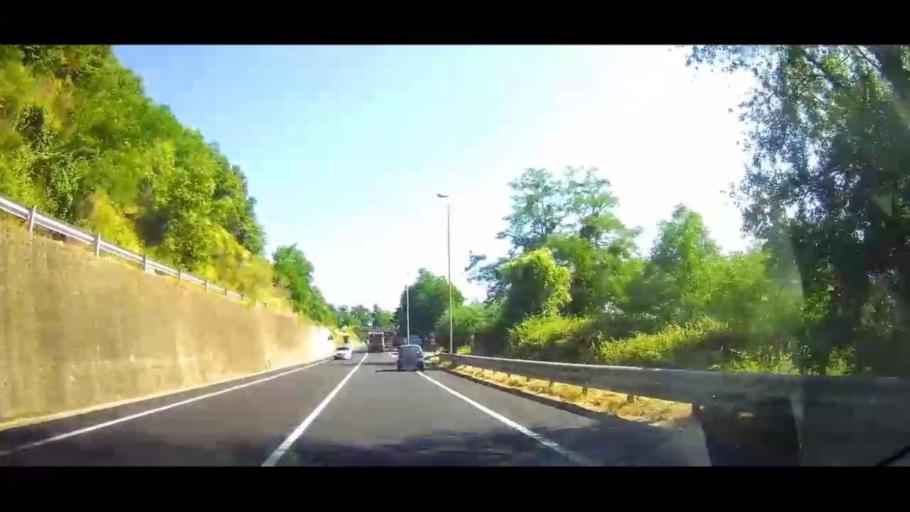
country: IT
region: Calabria
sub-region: Provincia di Cosenza
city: Spezzano della Sila
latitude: 39.2986
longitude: 16.3424
